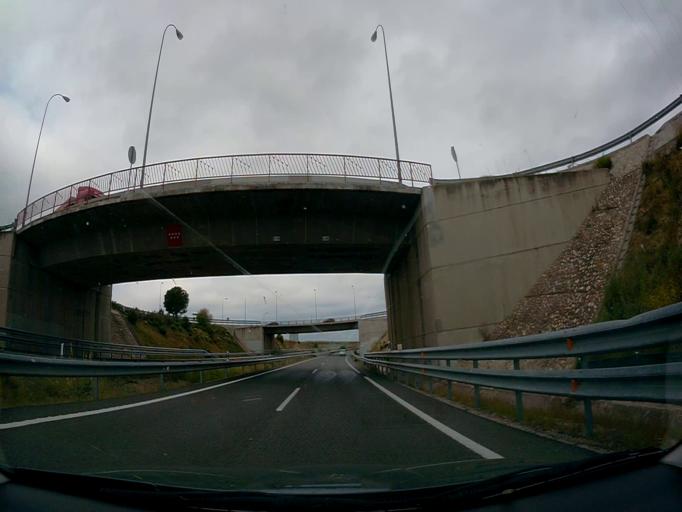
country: ES
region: Madrid
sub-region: Provincia de Madrid
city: Brunete
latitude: 40.3927
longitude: -3.9926
